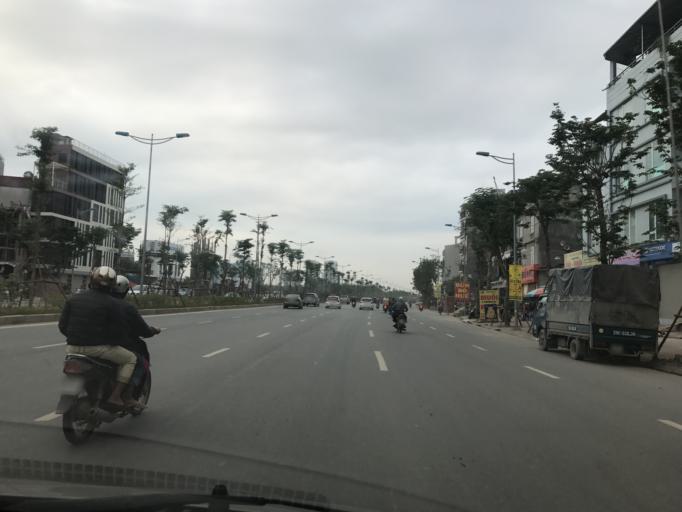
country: VN
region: Ha Noi
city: Cau Giay
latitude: 21.0501
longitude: 105.8047
